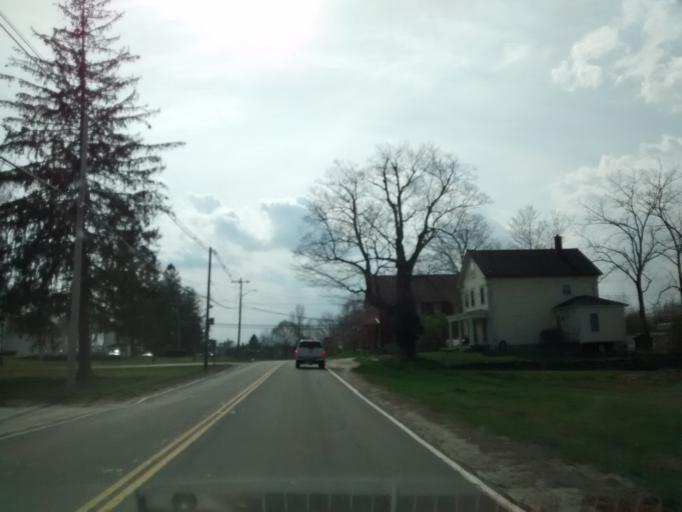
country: US
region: Massachusetts
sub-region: Worcester County
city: Sutton
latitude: 42.1505
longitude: -71.7614
